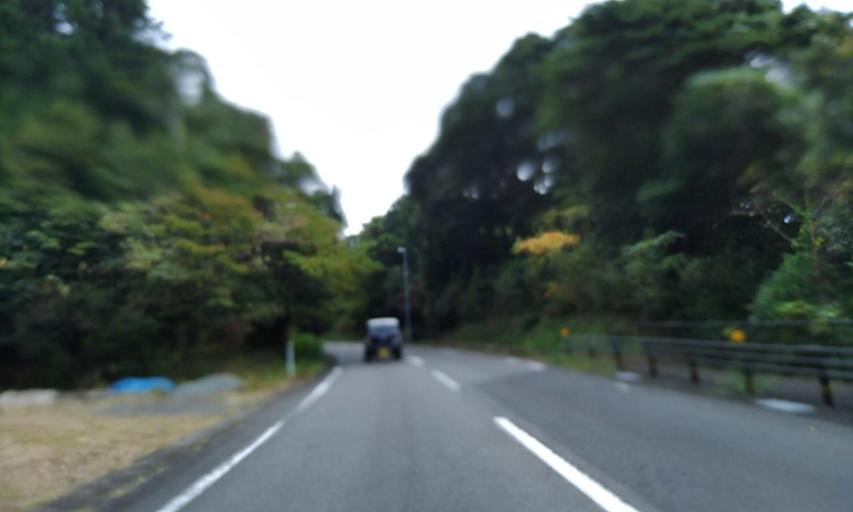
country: JP
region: Wakayama
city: Shingu
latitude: 33.4674
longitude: 135.8267
